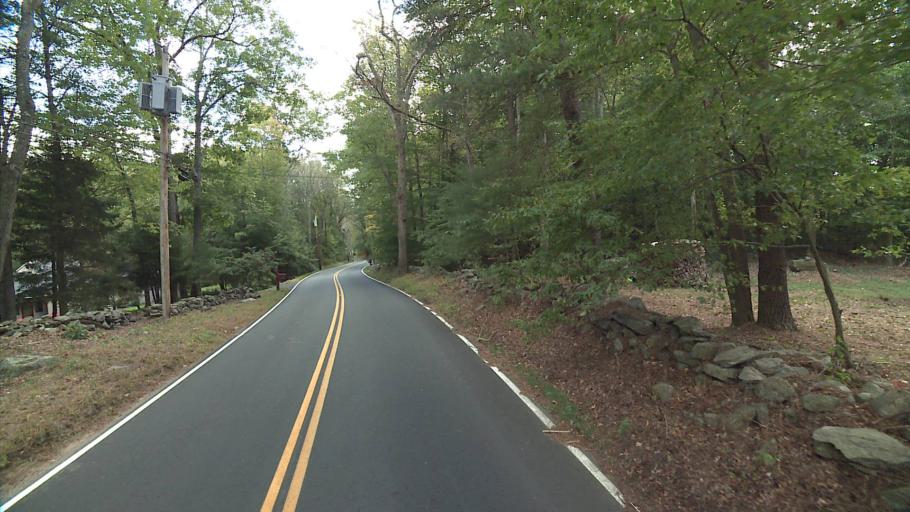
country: US
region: Connecticut
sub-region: New Haven County
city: Madison
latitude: 41.3848
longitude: -72.5935
